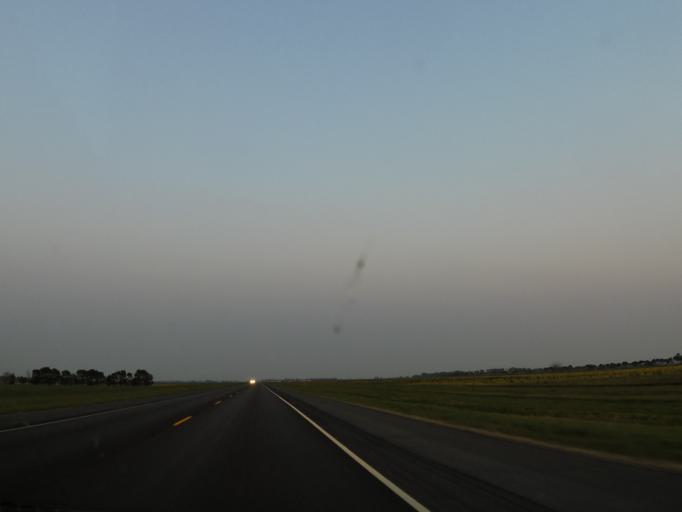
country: US
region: North Dakota
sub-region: Walsh County
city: Grafton
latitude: 48.4126
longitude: -97.5066
